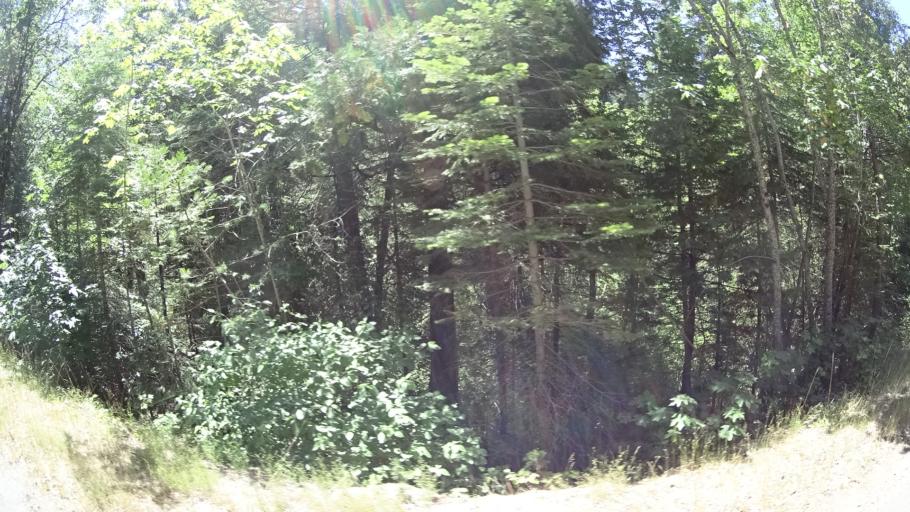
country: US
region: California
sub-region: Calaveras County
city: Arnold
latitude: 38.2203
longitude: -120.3387
